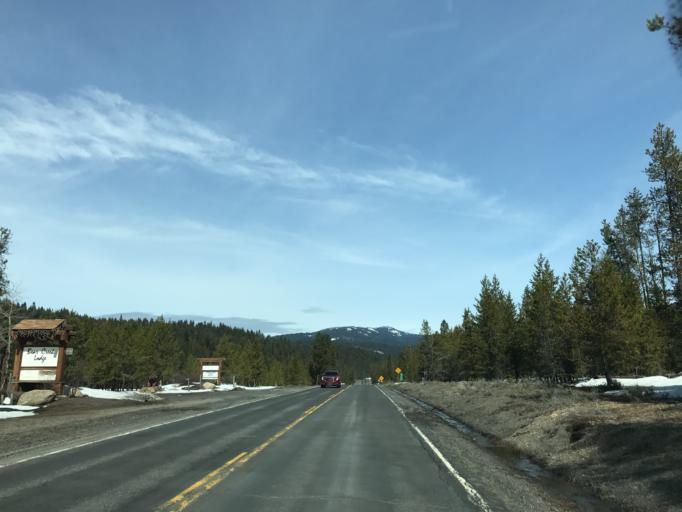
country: US
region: Idaho
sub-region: Valley County
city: McCall
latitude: 44.9489
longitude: -116.1685
